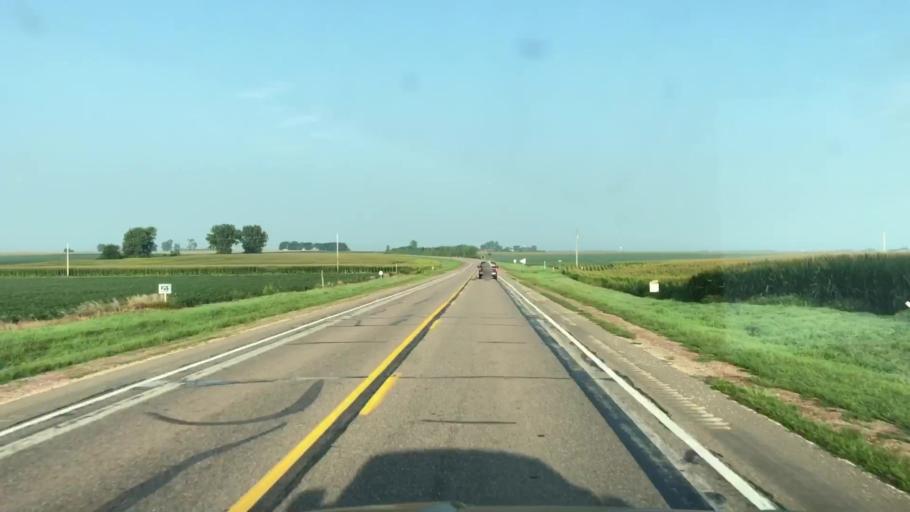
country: US
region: Iowa
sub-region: O'Brien County
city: Sheldon
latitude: 43.1861
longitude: -95.9391
